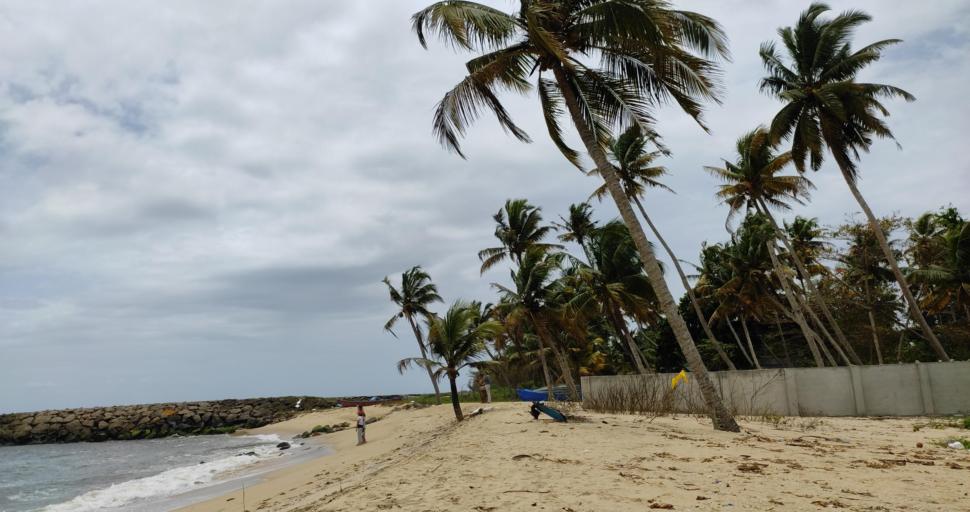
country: IN
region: Kerala
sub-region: Alappuzha
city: Vayalar
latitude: 9.6875
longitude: 76.2900
